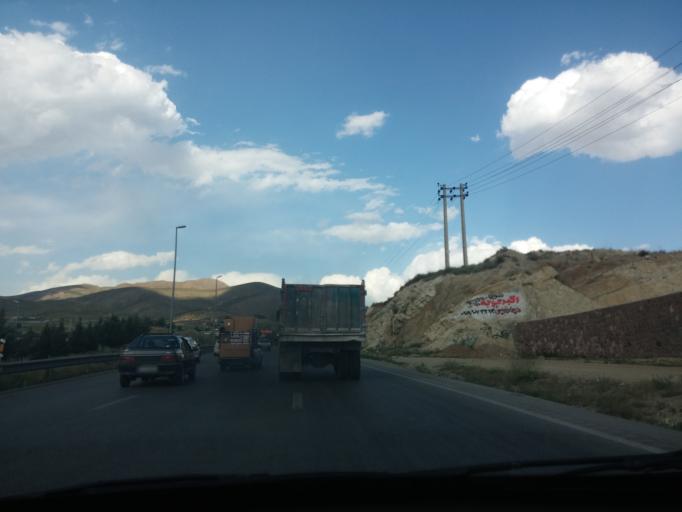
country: IR
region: Tehran
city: Damavand
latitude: 35.7173
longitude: 51.9347
